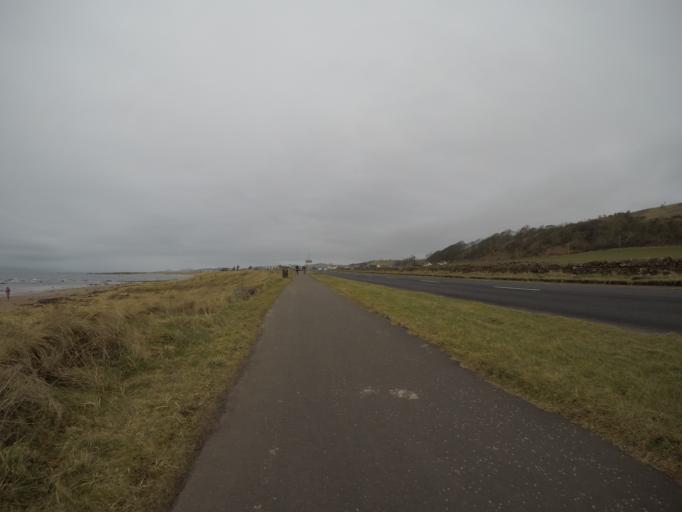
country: GB
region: Scotland
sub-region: North Ayrshire
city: West Kilbride
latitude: 55.6724
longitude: -4.8488
